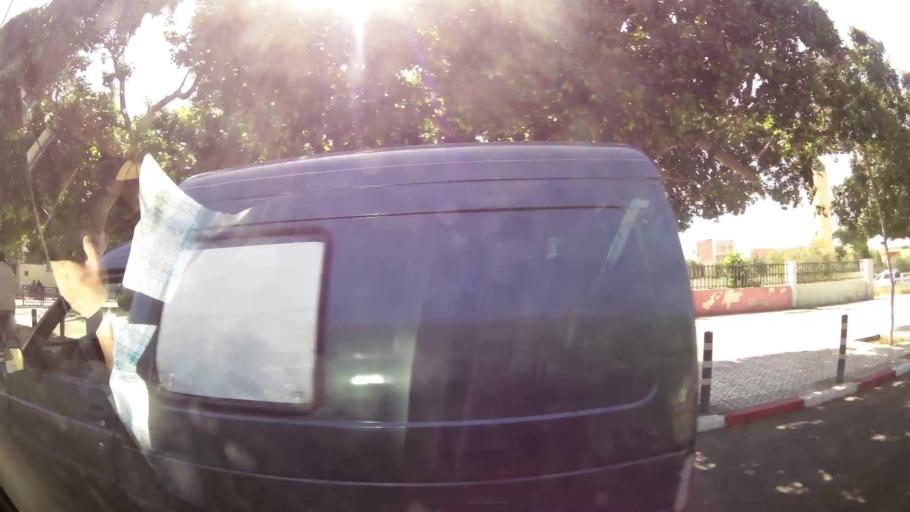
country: MA
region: Souss-Massa-Draa
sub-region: Inezgane-Ait Mellou
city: Inezgane
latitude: 30.3604
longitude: -9.5336
